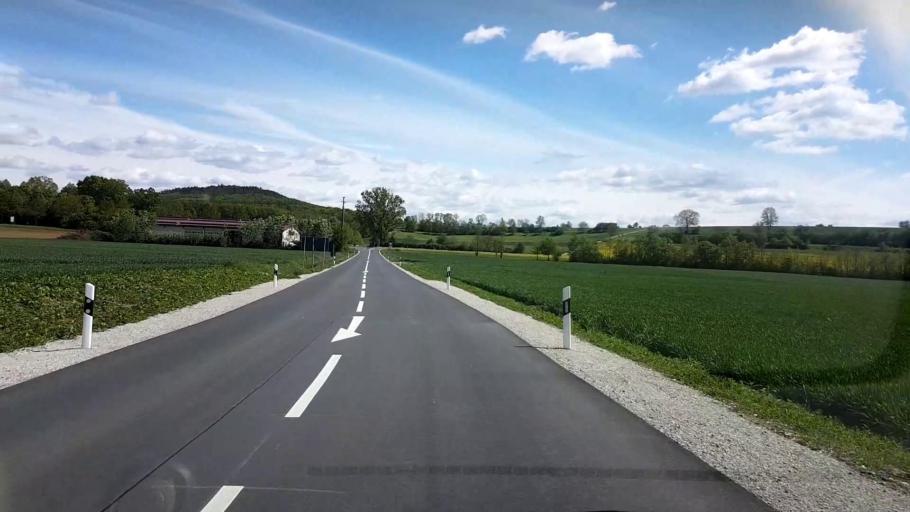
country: DE
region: Bavaria
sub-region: Upper Franconia
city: Buttenheim
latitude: 49.8052
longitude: 11.0411
